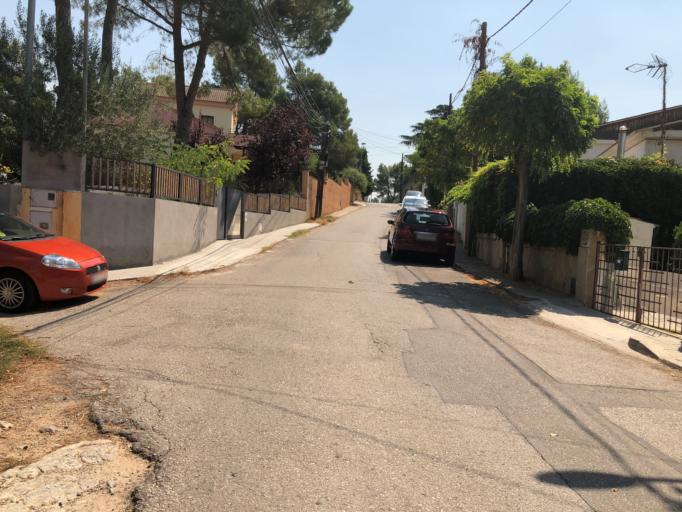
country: ES
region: Catalonia
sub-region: Provincia de Barcelona
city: Corbera de Llobregat
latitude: 41.4165
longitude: 1.9114
